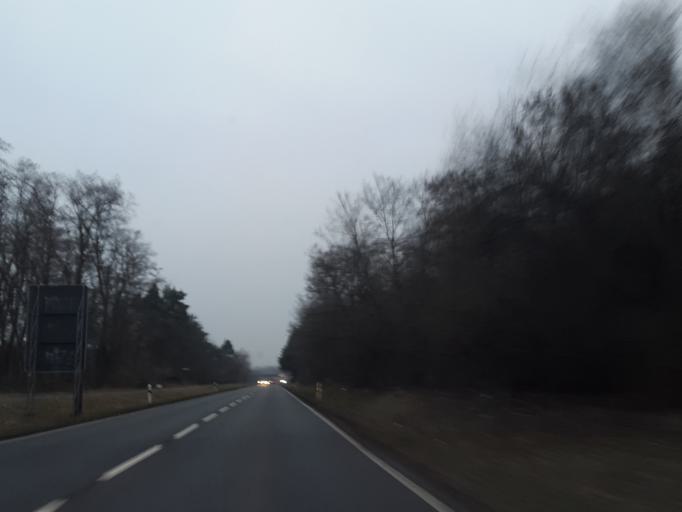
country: DE
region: Bavaria
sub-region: Regierungsbezirk Unterfranken
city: Kleinostheim
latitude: 50.0160
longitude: 9.0514
